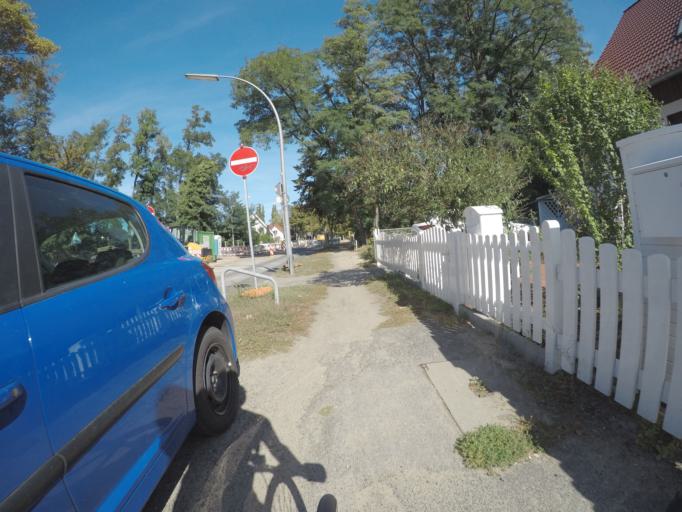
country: DE
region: Berlin
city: Heiligensee
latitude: 52.6212
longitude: 13.2236
